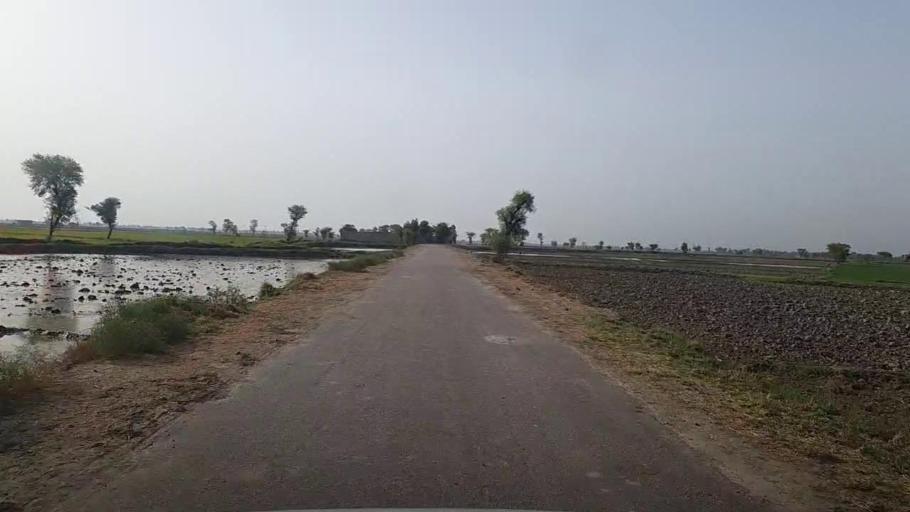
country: PK
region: Sindh
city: Khairpur Nathan Shah
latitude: 27.0977
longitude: 67.7937
